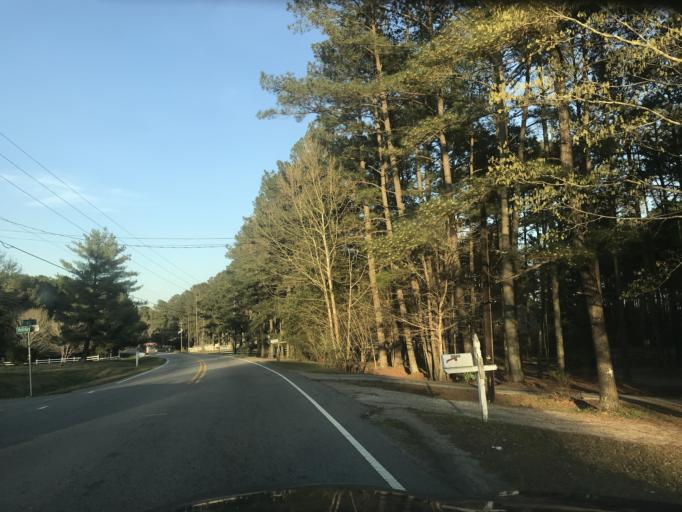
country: US
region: North Carolina
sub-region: Wake County
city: Garner
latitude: 35.7395
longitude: -78.5457
